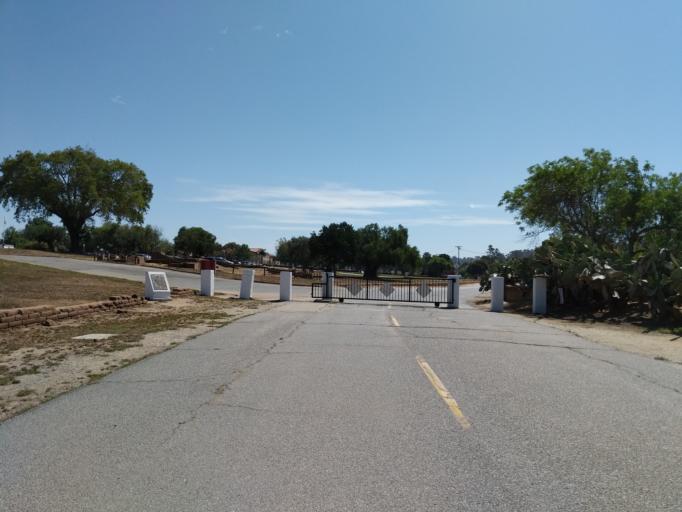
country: US
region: California
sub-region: San Diego County
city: Camp Pendleton South
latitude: 33.2311
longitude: -117.3207
